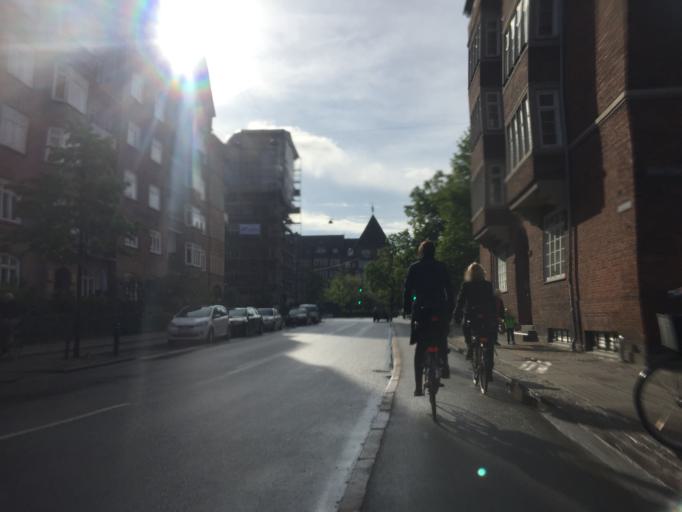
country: DK
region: Capital Region
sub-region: Kobenhavn
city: Copenhagen
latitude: 55.6792
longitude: 12.5513
